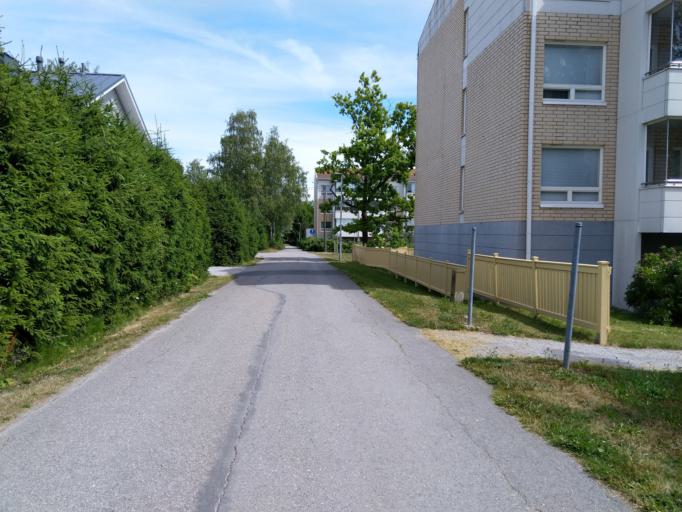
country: FI
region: Varsinais-Suomi
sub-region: Salo
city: Halikko
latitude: 60.3992
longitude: 23.0763
